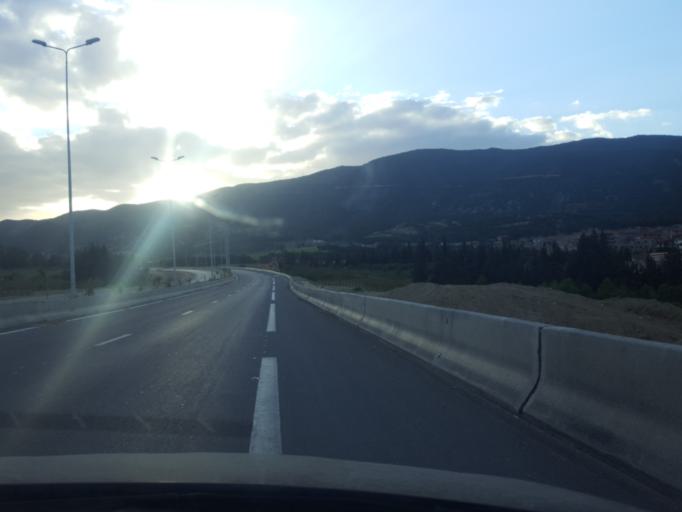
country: TN
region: Tunis
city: Hammam-Lif
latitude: 36.6897
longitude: 10.3931
